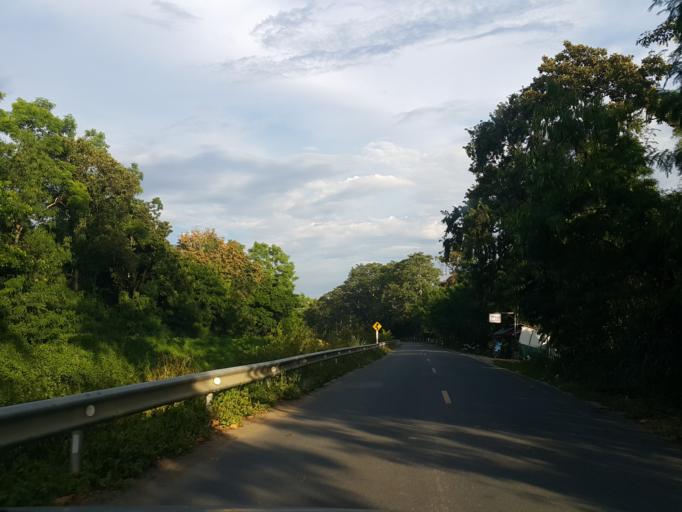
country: TH
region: Chiang Mai
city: San Sai
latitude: 18.9185
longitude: 99.0029
